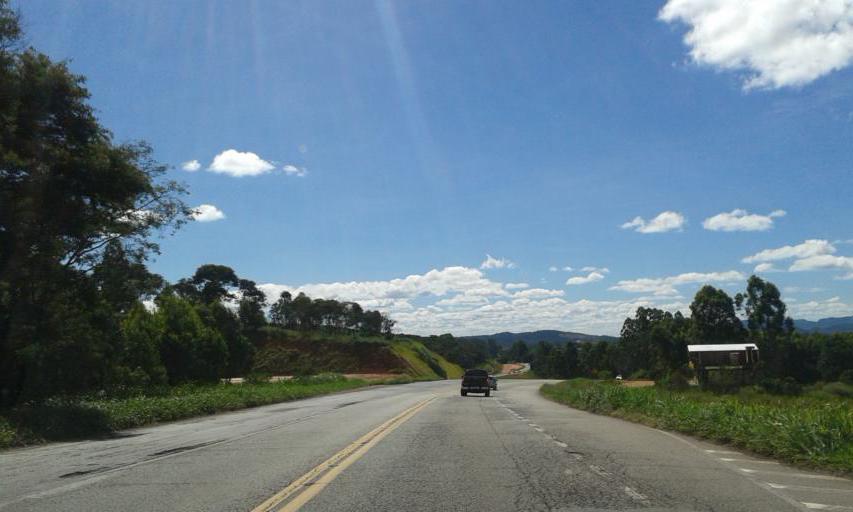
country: BR
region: Minas Gerais
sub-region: Caete
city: Caete
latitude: -19.7508
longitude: -43.5424
